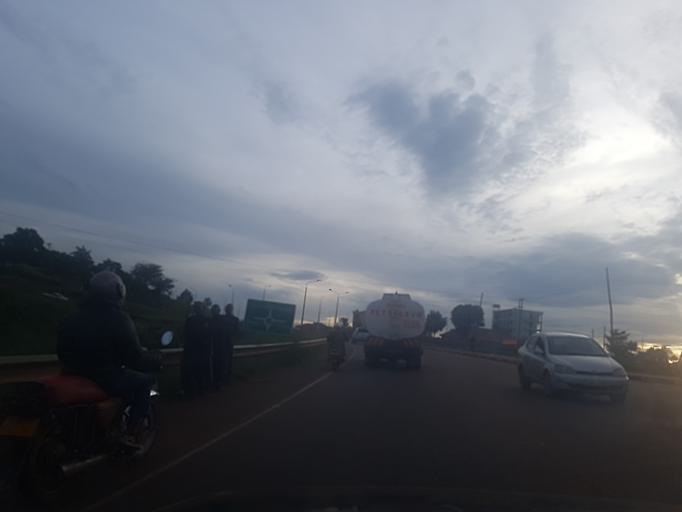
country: UG
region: Central Region
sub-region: Wakiso District
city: Kireka
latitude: 0.3659
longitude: 32.6064
